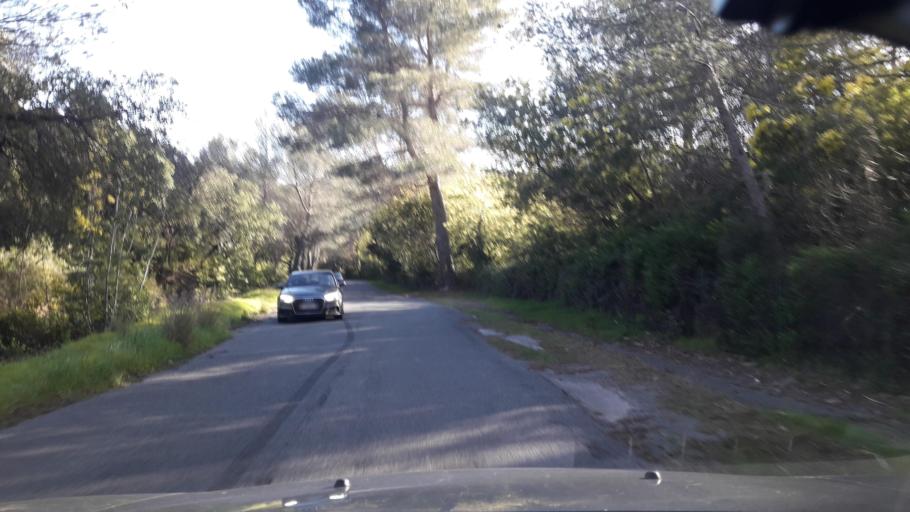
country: FR
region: Provence-Alpes-Cote d'Azur
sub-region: Departement du Var
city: Saint-Raphael
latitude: 43.4236
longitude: 6.8229
